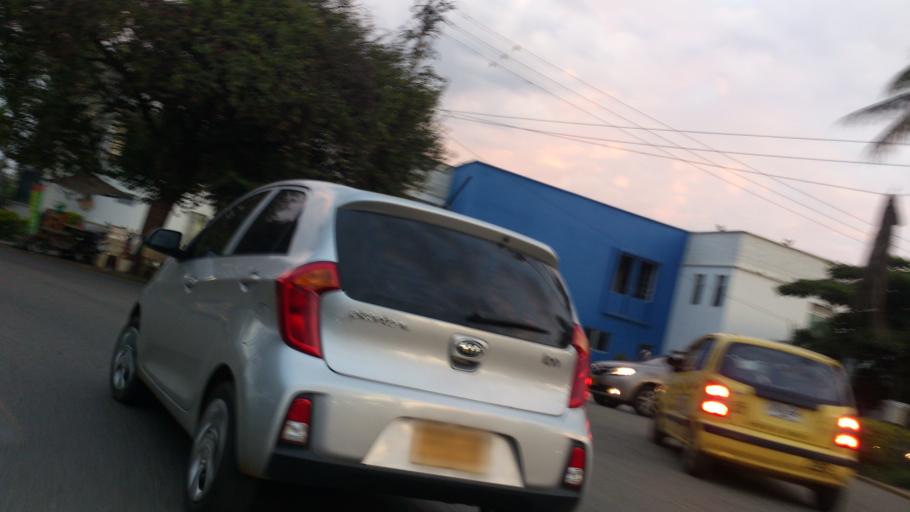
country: CO
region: Valle del Cauca
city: Jamundi
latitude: 3.2579
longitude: -76.5448
